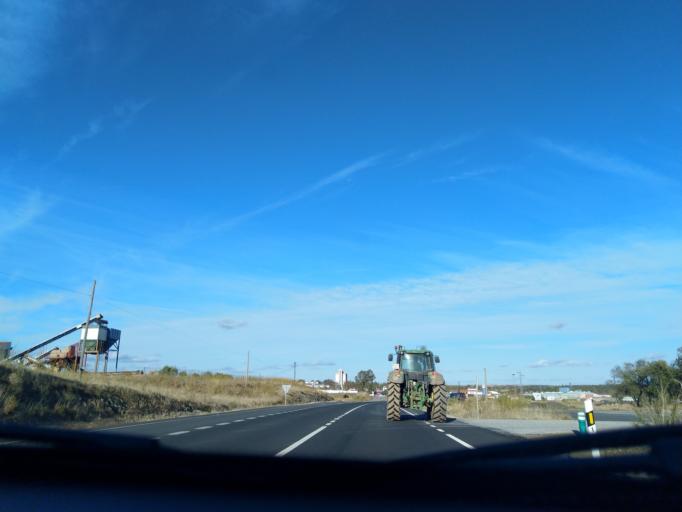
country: ES
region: Extremadura
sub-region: Provincia de Badajoz
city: Ahillones
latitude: 38.2734
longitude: -5.8330
